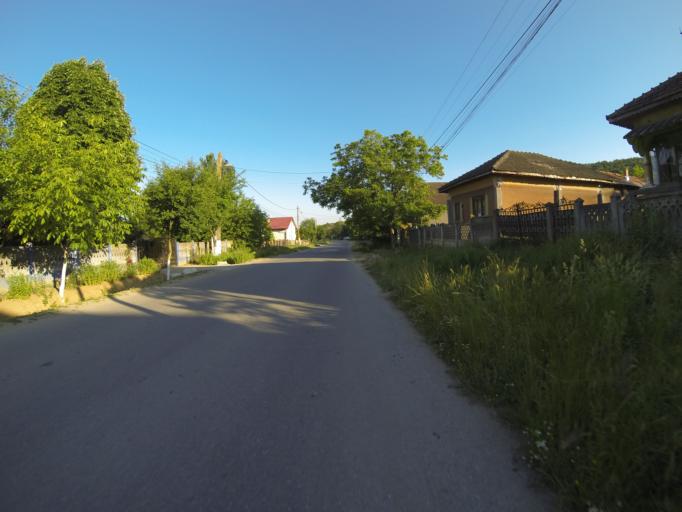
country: RO
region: Dolj
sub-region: Comuna Tuglui
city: Tuglui
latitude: 44.2111
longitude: 23.7937
